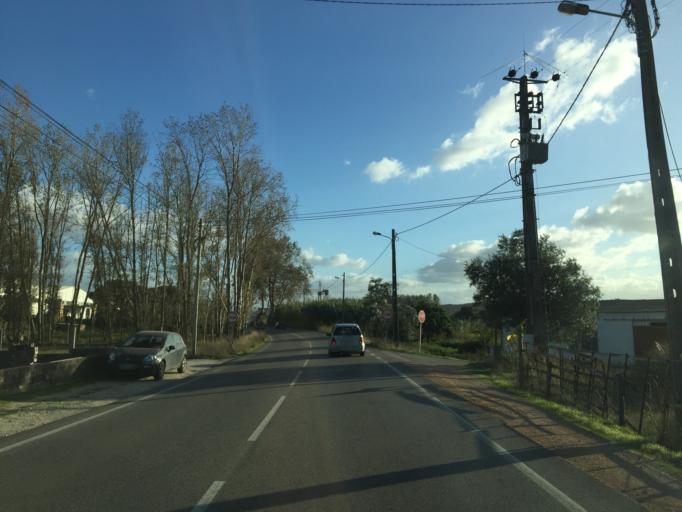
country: PT
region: Leiria
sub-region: Leiria
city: Amor
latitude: 39.8051
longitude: -8.8396
